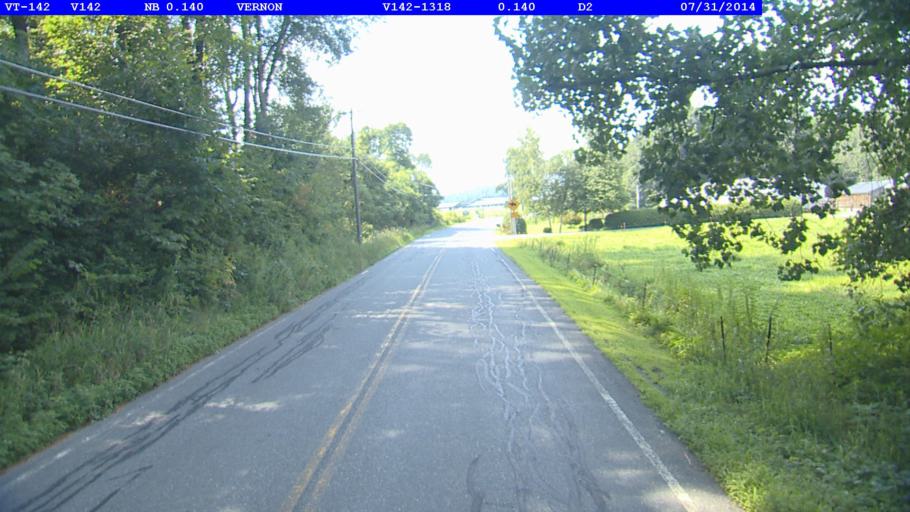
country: US
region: Massachusetts
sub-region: Franklin County
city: Northfield
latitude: 42.7286
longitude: -72.4665
